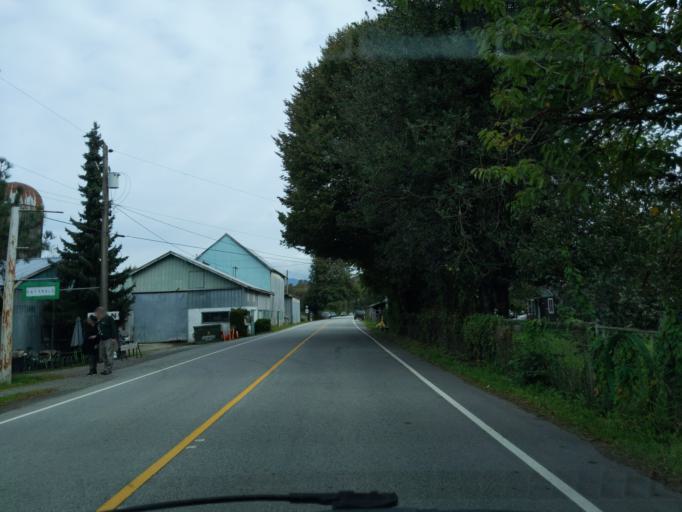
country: CA
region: British Columbia
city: Maple Ridge
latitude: 49.2046
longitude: -122.6241
